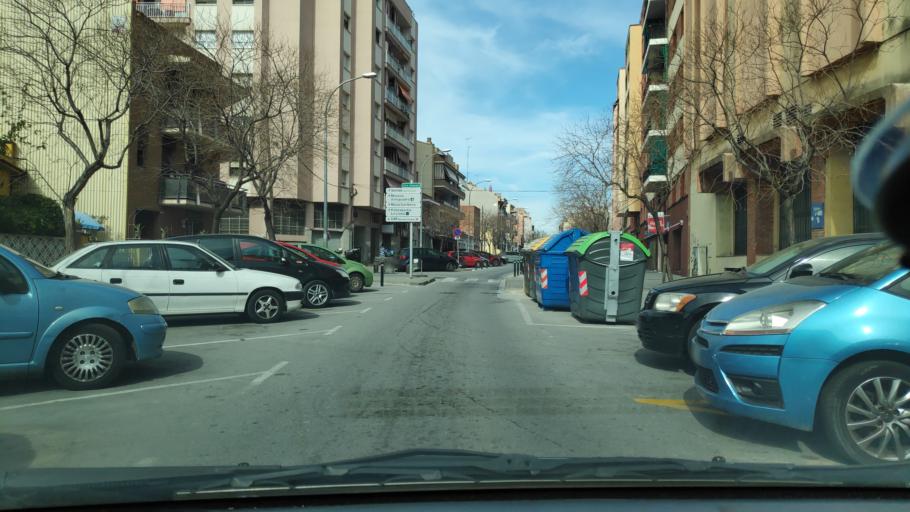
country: ES
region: Catalonia
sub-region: Provincia de Barcelona
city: Rubi
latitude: 41.4976
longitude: 2.0322
